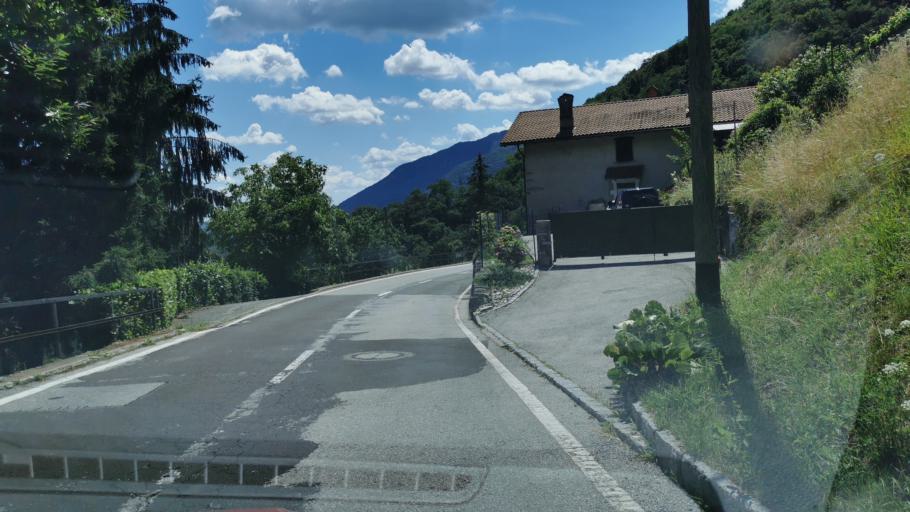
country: IT
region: Lombardy
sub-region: Provincia di Como
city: Campione
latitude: 45.9519
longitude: 8.9825
